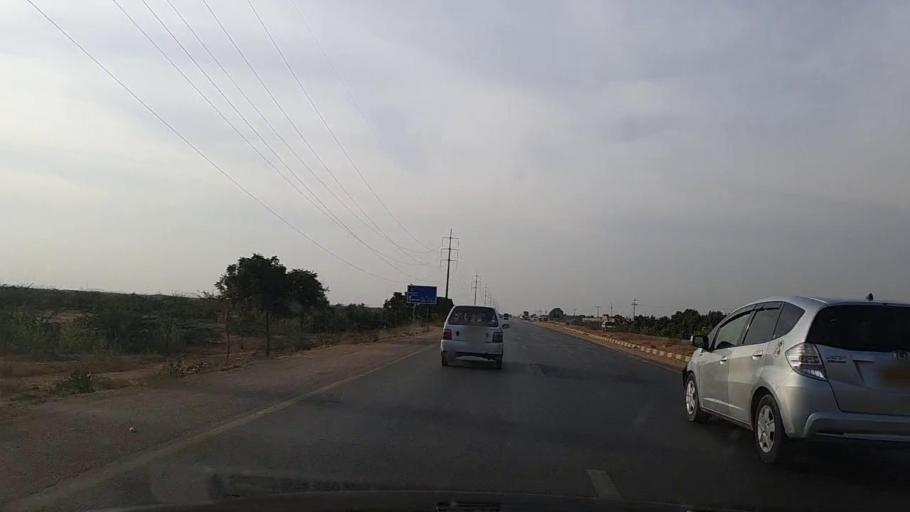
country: PK
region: Sindh
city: Gharo
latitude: 24.8278
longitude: 67.4699
